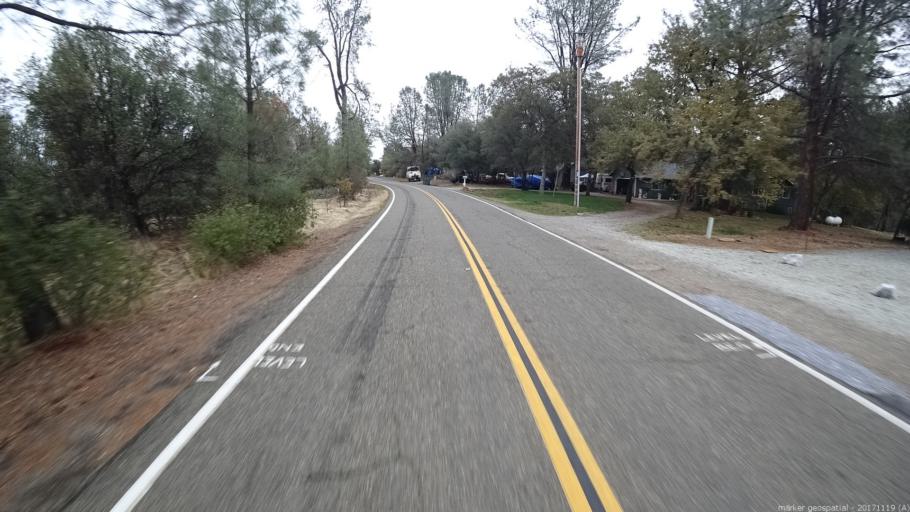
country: US
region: California
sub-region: Shasta County
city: Redding
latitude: 40.4855
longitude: -122.4487
